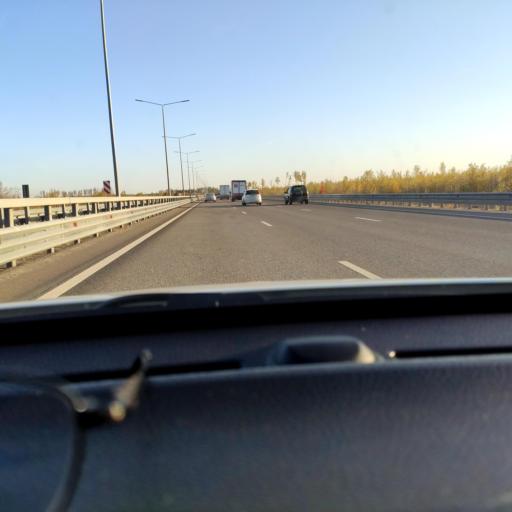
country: RU
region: Voronezj
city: Somovo
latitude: 51.7706
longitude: 39.3018
